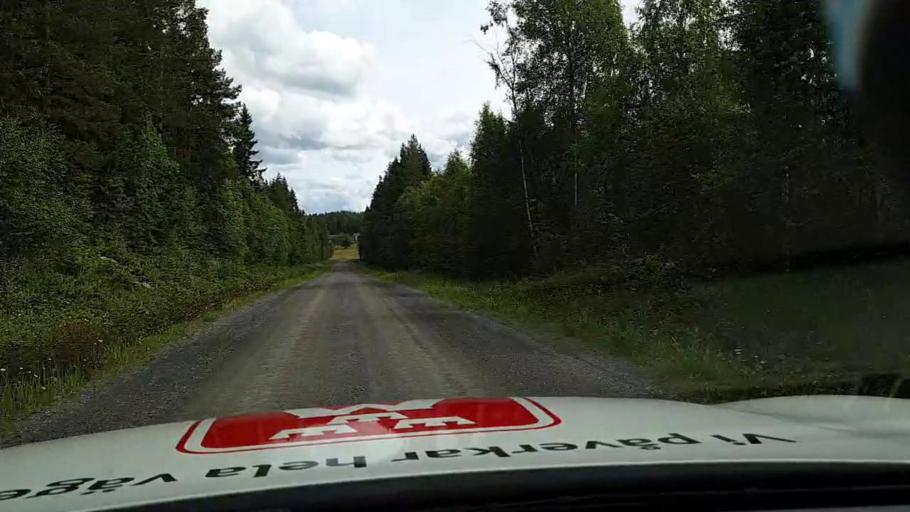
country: SE
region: Jaemtland
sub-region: Braecke Kommun
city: Braecke
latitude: 63.2864
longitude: 15.3635
